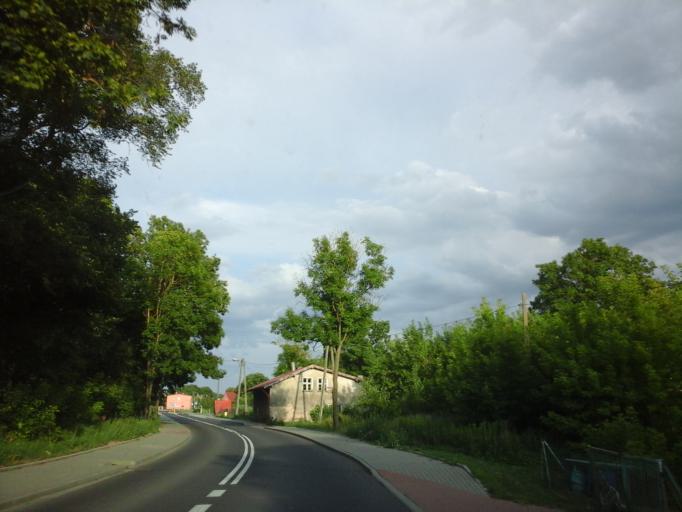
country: PL
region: West Pomeranian Voivodeship
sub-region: Powiat kamienski
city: Golczewo
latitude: 53.8488
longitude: 14.9477
